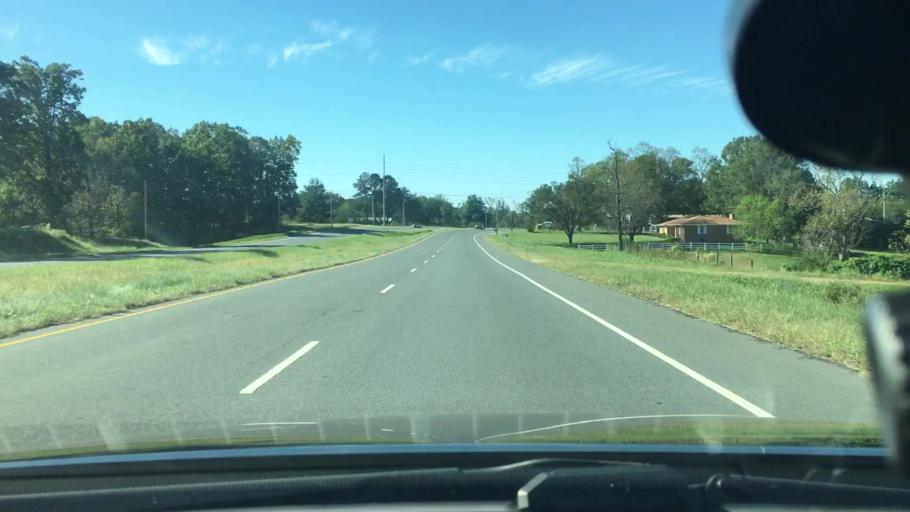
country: US
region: North Carolina
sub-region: Stanly County
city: Oakboro
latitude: 35.2906
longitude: -80.2907
